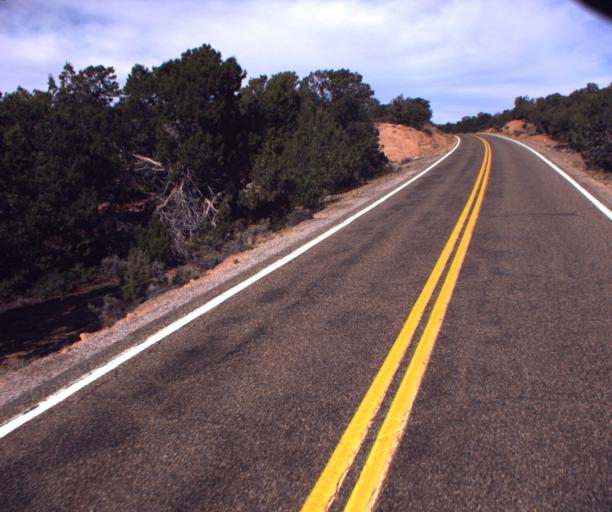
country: US
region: Arizona
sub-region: Navajo County
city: Kayenta
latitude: 36.6400
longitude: -110.5117
